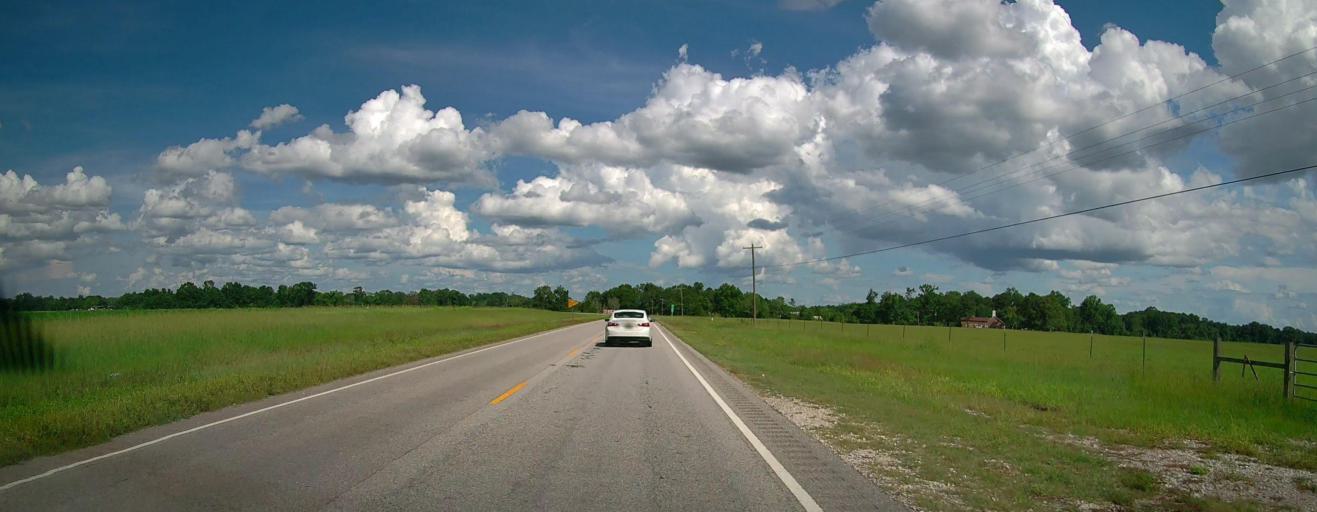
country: US
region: Alabama
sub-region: Lee County
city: Auburn
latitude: 32.4270
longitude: -85.4569
